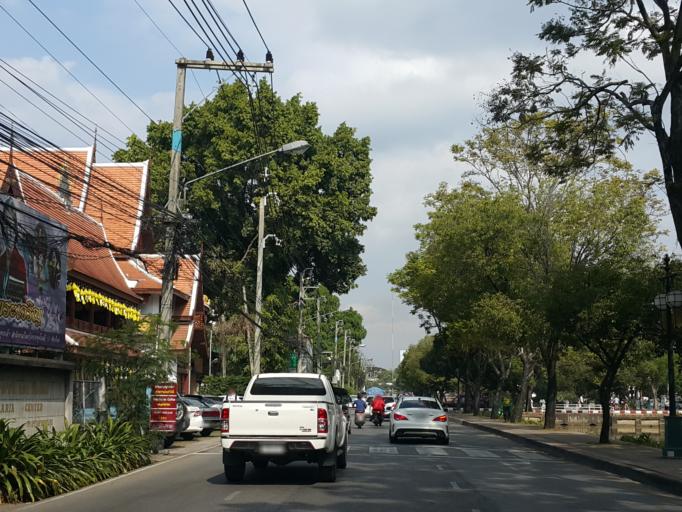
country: TH
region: Chiang Mai
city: Chiang Mai
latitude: 18.7920
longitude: 98.9780
